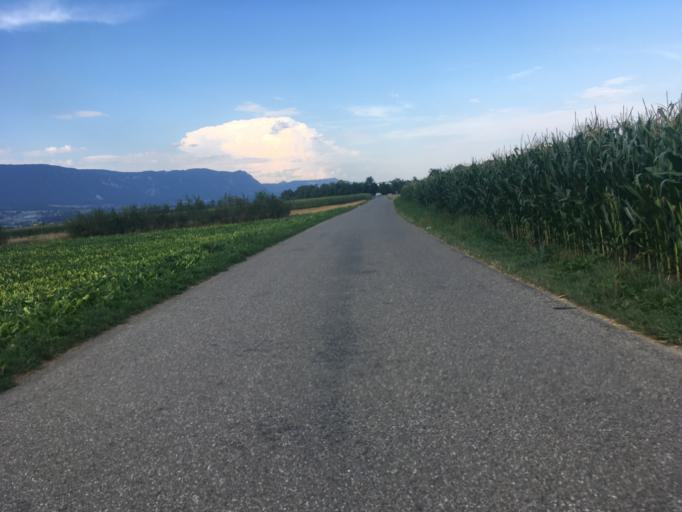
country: CH
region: Bern
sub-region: Seeland District
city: Arch
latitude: 47.1680
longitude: 7.4110
